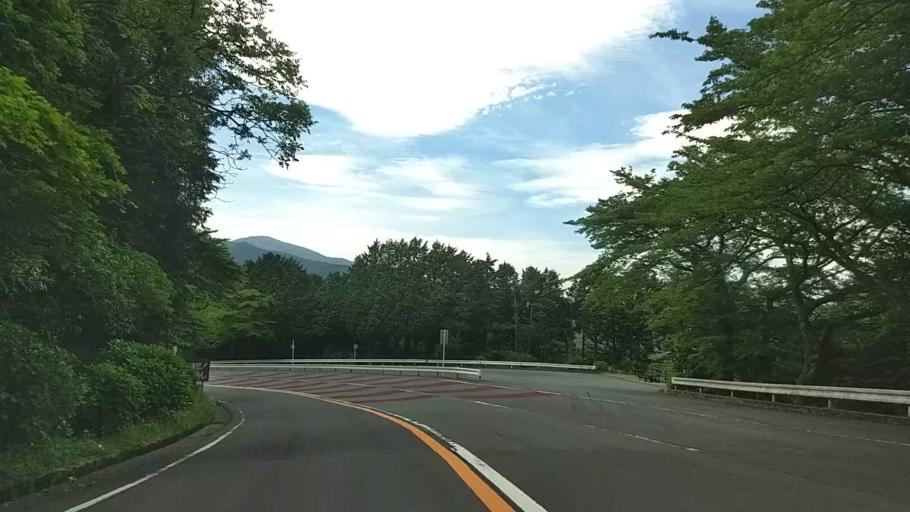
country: JP
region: Kanagawa
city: Odawara
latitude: 35.2190
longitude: 139.1162
